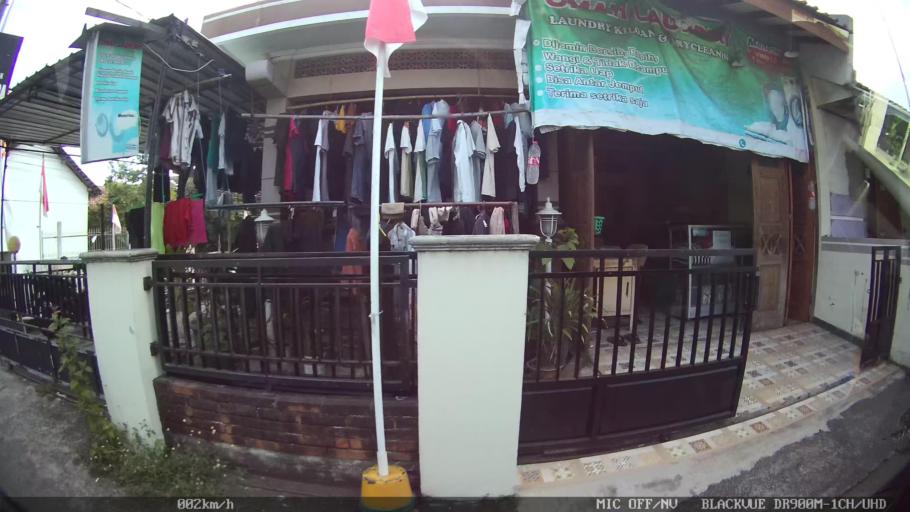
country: ID
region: Daerah Istimewa Yogyakarta
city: Yogyakarta
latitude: -7.7888
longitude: 110.3512
